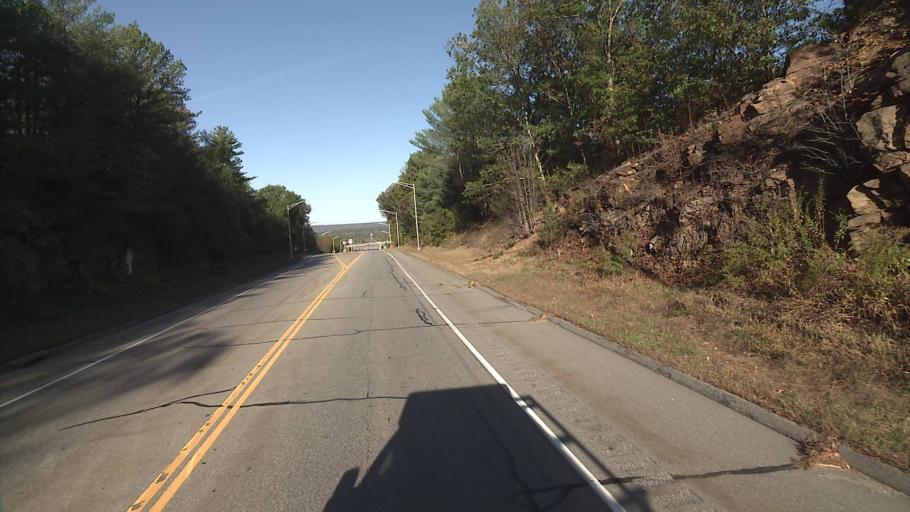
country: US
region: Connecticut
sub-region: Windham County
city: Danielson
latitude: 41.7904
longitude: -71.8701
